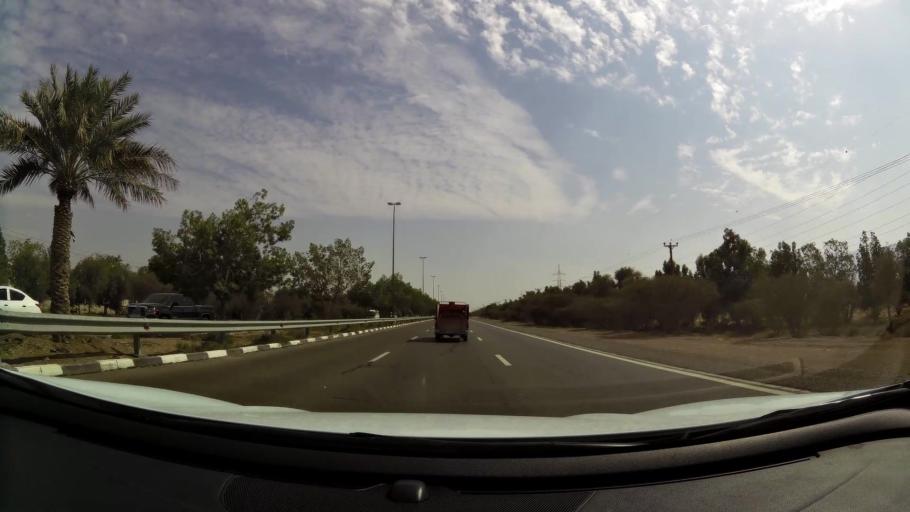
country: AE
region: Abu Dhabi
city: Al Ain
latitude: 24.1337
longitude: 55.8181
